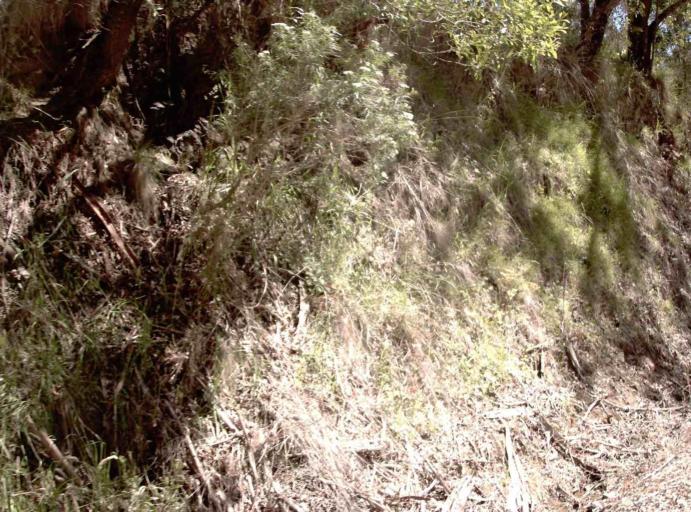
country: AU
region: Victoria
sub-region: East Gippsland
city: Lakes Entrance
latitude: -37.2224
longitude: 148.2640
